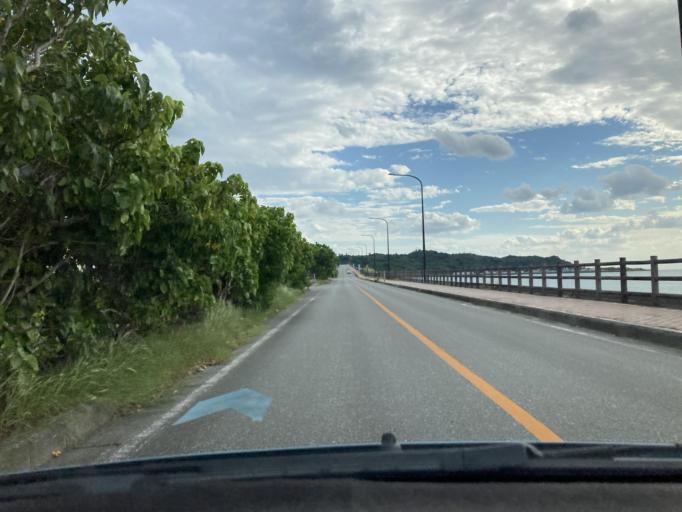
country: JP
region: Okinawa
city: Katsuren-haebaru
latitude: 26.3392
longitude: 127.9547
